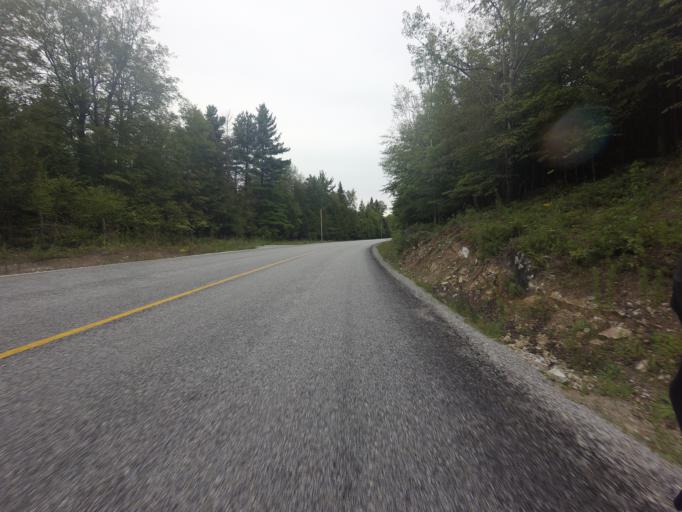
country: CA
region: Ontario
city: Perth
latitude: 44.9051
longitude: -76.4935
